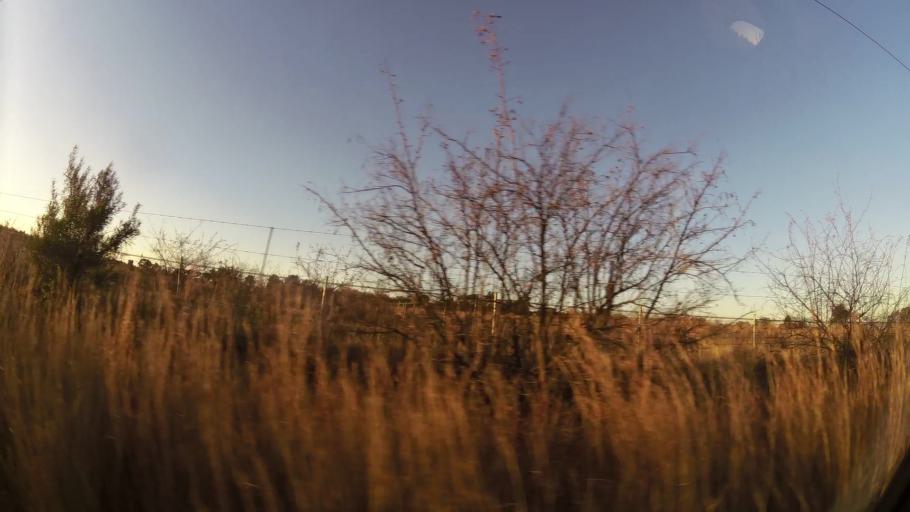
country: ZA
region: Gauteng
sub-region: City of Johannesburg Metropolitan Municipality
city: Diepsloot
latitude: -25.9515
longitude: 28.0562
